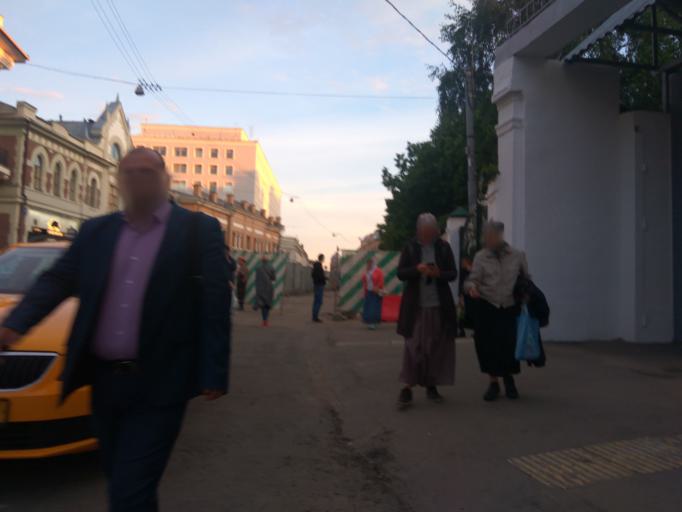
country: RU
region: Moscow
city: Moscow
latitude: 55.7658
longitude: 37.6310
